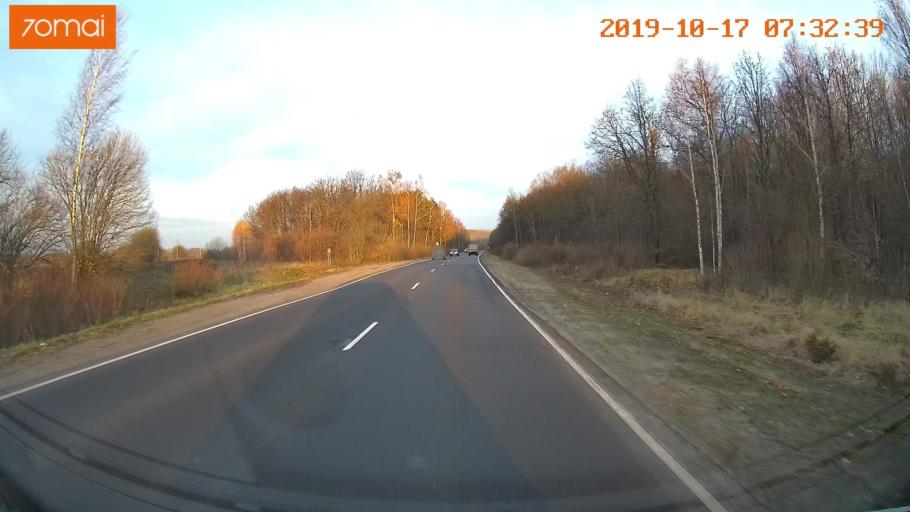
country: RU
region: Ivanovo
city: Gavrilov Posad
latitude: 56.3983
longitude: 39.9704
